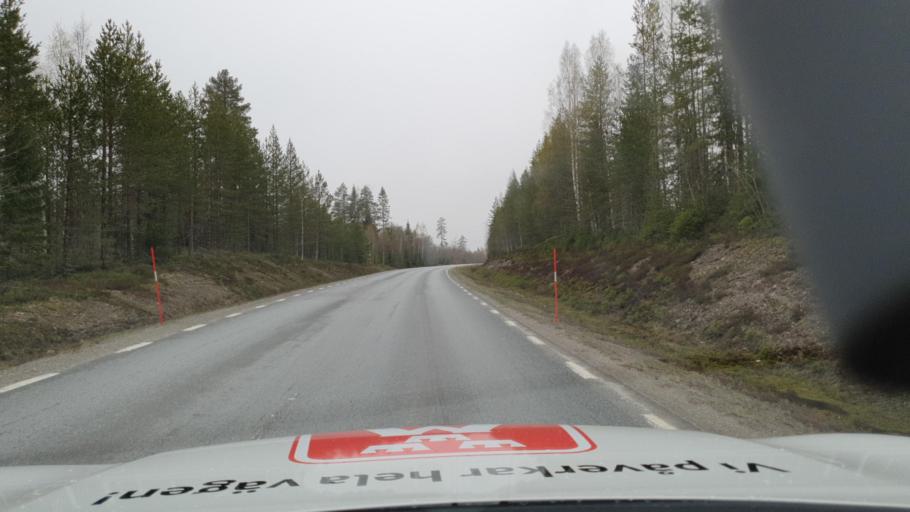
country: SE
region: Vaesterbotten
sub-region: Vannas Kommun
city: Vaennaes
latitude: 63.7801
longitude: 19.7360
